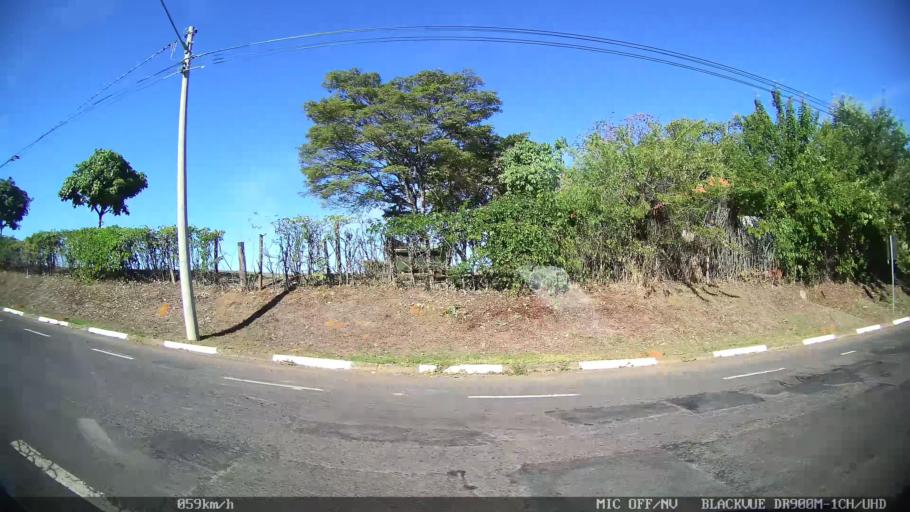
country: BR
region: Sao Paulo
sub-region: Franca
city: Franca
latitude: -20.5644
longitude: -47.3618
